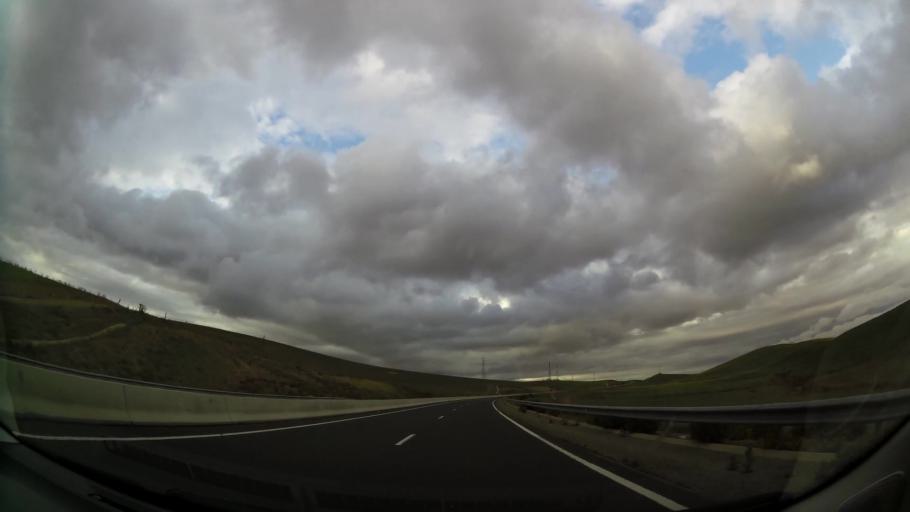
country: MA
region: Taza-Al Hoceima-Taounate
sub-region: Taza
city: Taza
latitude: 34.2665
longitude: -3.8423
